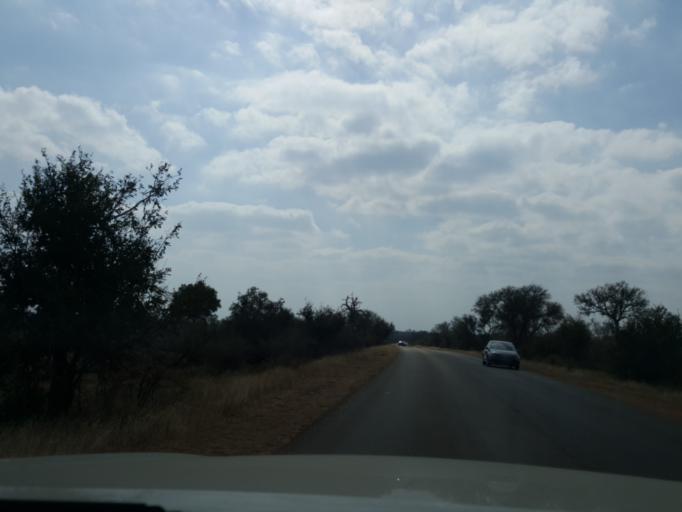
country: ZA
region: Mpumalanga
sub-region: Ehlanzeni District
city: Komatipoort
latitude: -25.3287
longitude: 31.8800
